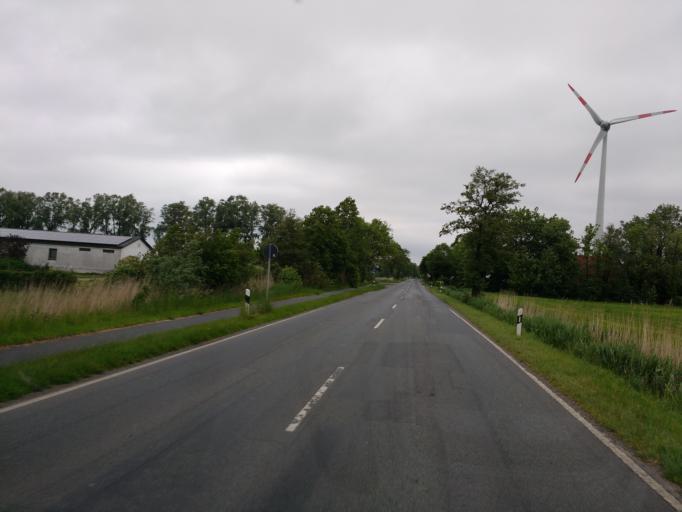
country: DE
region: Lower Saxony
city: Jever
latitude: 53.5906
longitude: 7.9162
